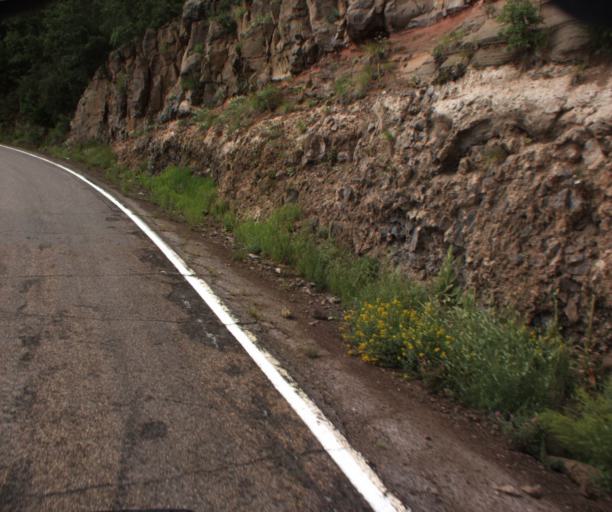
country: US
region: Arizona
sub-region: Greenlee County
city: Morenci
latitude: 33.5686
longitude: -109.3488
